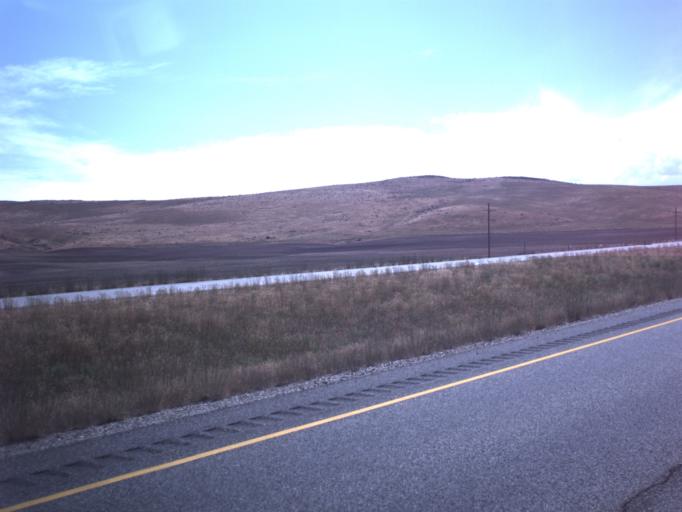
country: US
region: Utah
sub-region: Box Elder County
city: Garland
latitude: 41.8932
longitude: -112.5204
